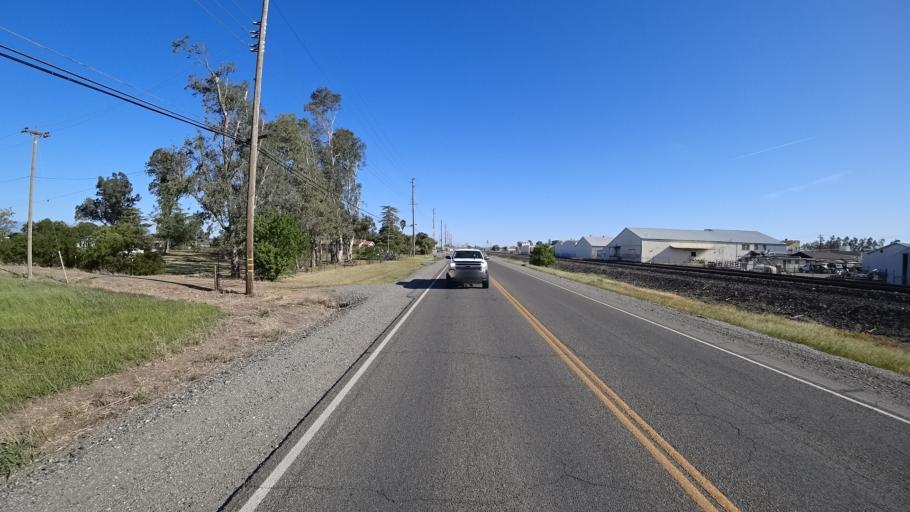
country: US
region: California
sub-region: Glenn County
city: Orland
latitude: 39.7354
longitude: -122.1969
